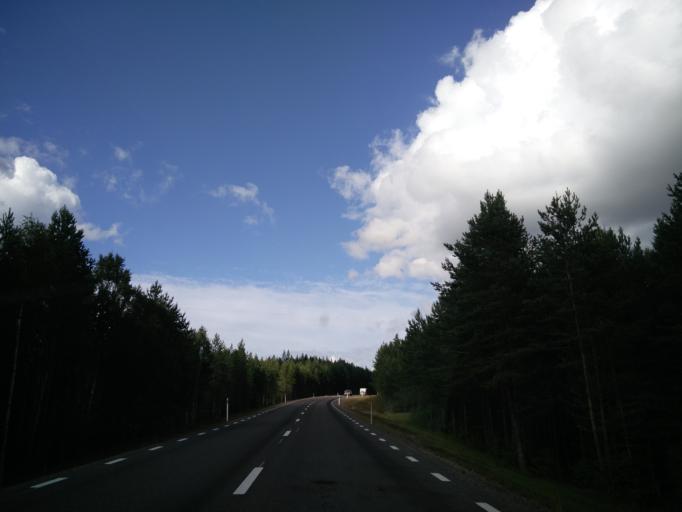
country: SE
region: Vaermland
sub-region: Torsby Kommun
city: Torsby
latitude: 60.3715
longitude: 13.2053
